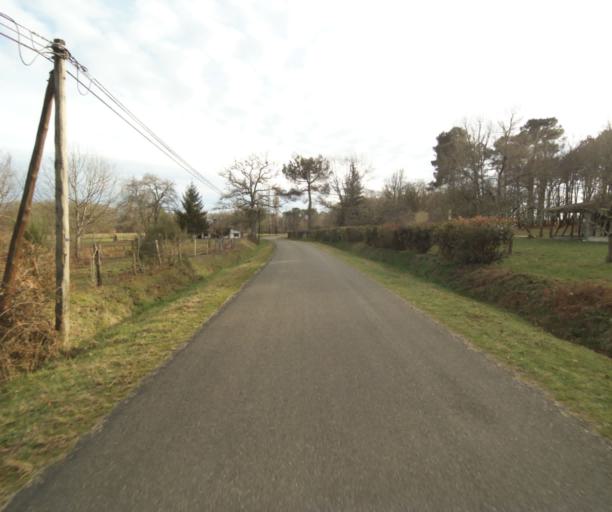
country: FR
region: Aquitaine
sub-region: Departement des Landes
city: Gabarret
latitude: 44.0236
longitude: 0.0475
